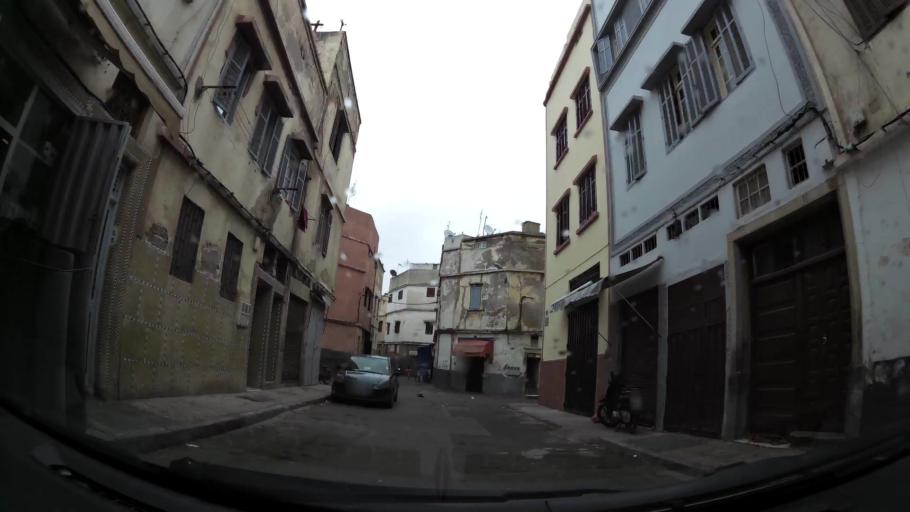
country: MA
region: Grand Casablanca
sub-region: Casablanca
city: Casablanca
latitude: 33.5686
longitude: -7.6066
